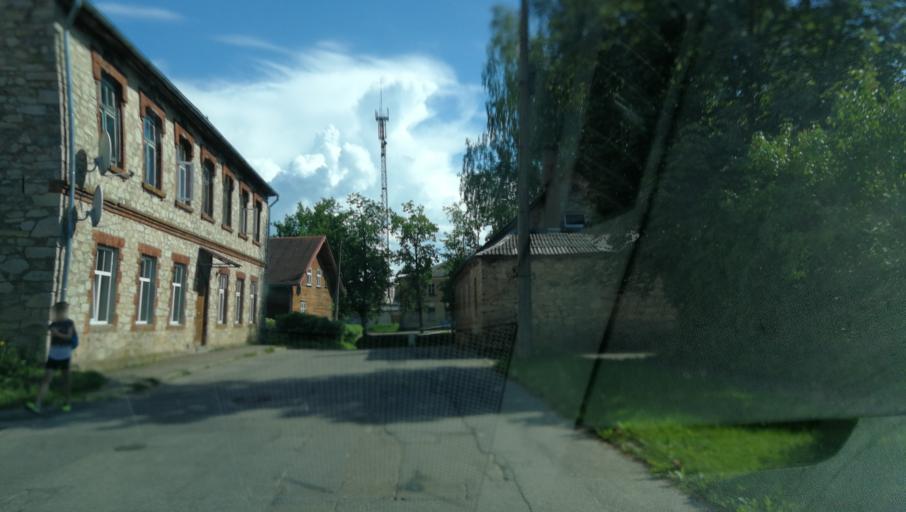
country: LV
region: Cesu Rajons
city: Cesis
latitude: 57.3091
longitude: 25.2578
